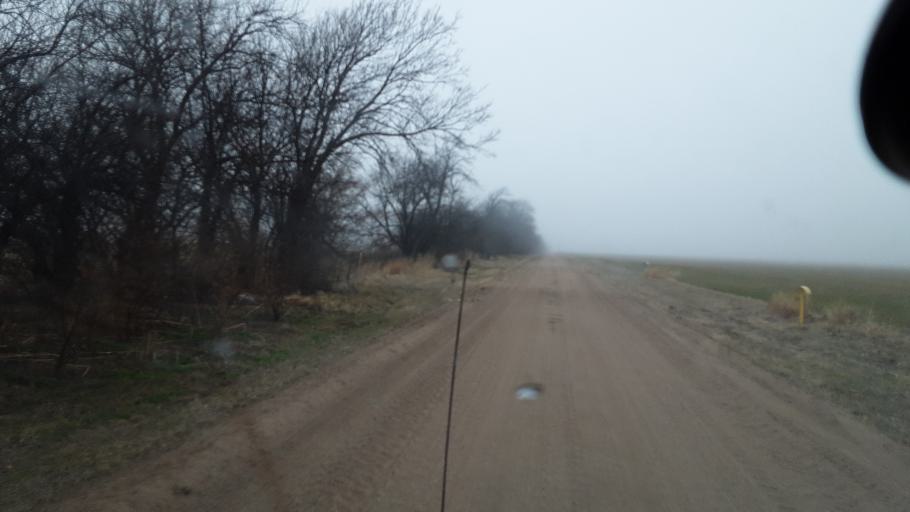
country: US
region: Kansas
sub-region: Reno County
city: South Hutchinson
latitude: 37.9552
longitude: -97.9607
